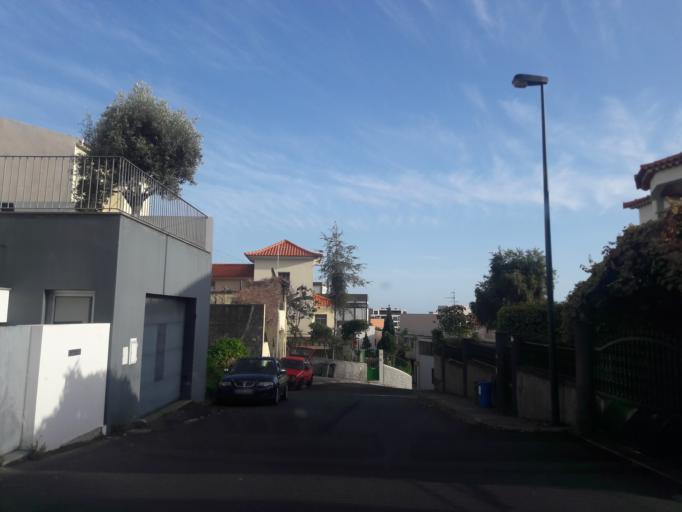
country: PT
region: Madeira
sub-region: Funchal
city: Nossa Senhora do Monte
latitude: 32.6581
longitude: -16.9303
